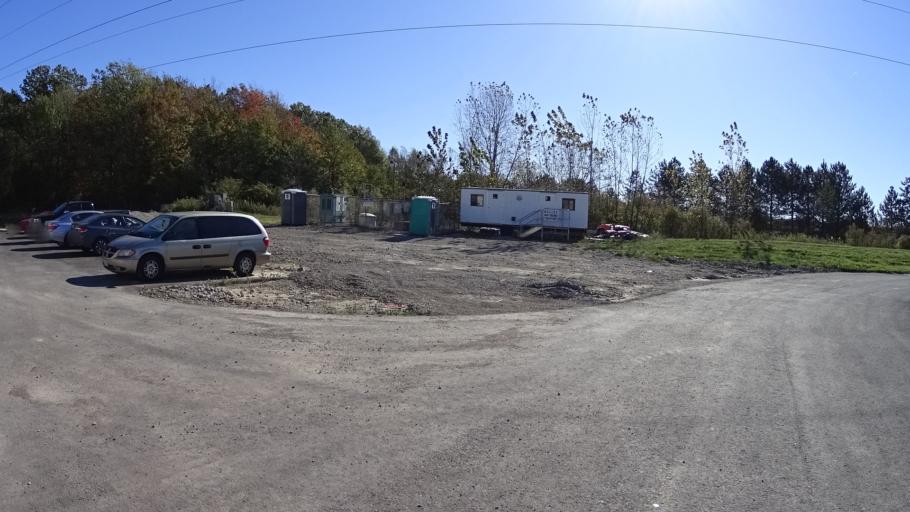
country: US
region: Ohio
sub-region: Lorain County
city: Amherst
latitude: 41.4225
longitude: -82.2130
